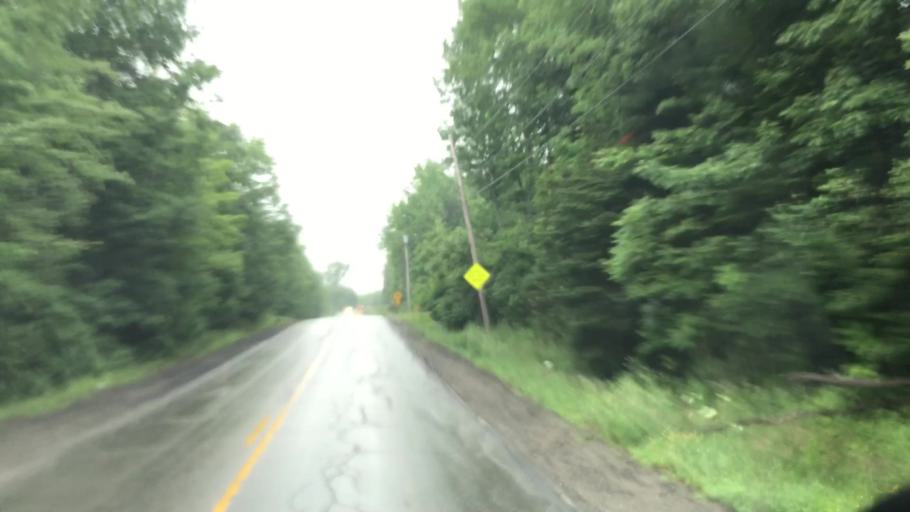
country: US
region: Maine
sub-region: Penobscot County
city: Veazie
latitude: 44.8757
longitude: -68.7133
